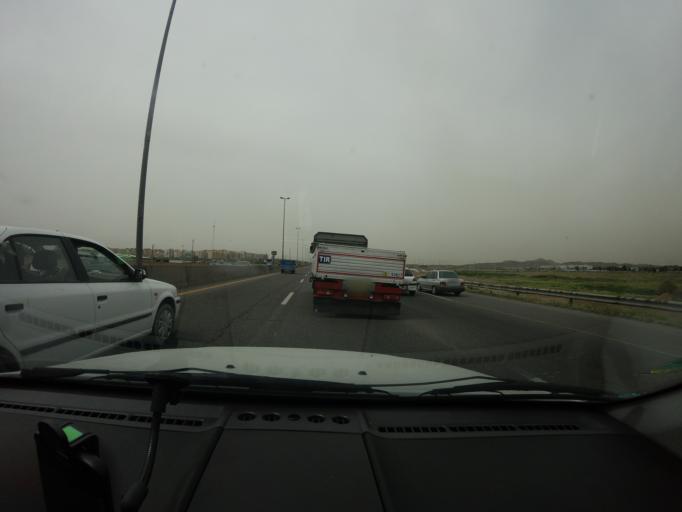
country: IR
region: Tehran
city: Robat Karim
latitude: 35.4931
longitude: 51.0561
